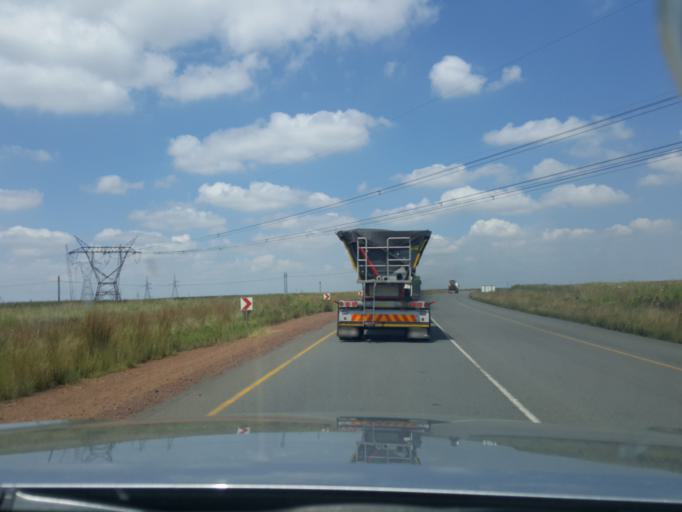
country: ZA
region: Mpumalanga
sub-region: Nkangala District Municipality
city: Witbank
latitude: -26.0150
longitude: 29.4185
